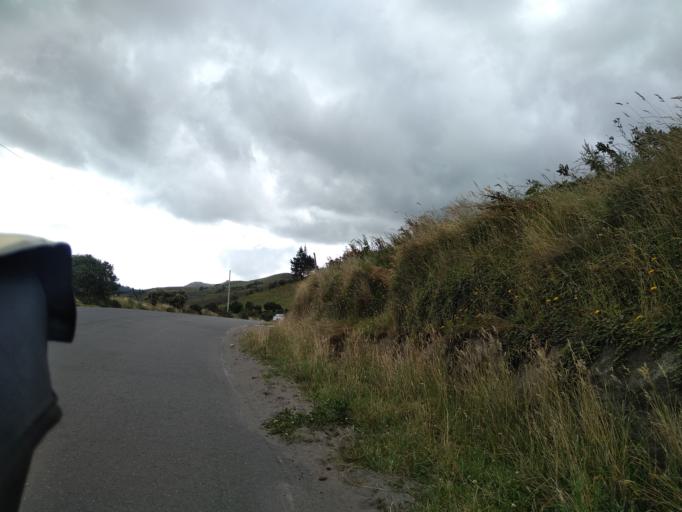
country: EC
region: Cotopaxi
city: Saquisili
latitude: -0.7216
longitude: -78.7618
